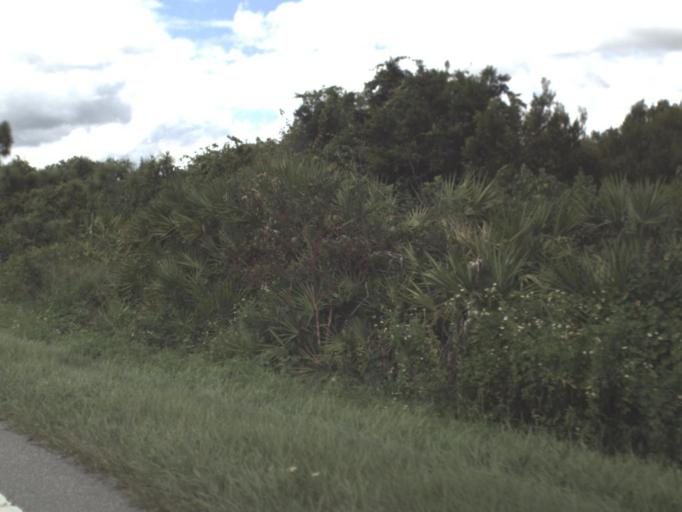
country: US
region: Florida
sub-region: Hillsborough County
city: Balm
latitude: 27.6355
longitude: -82.0671
